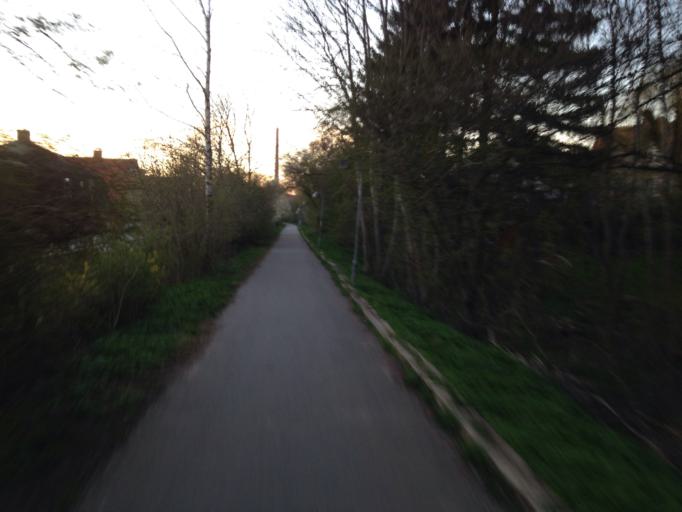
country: DK
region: Capital Region
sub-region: Hillerod Kommune
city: Hillerod
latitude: 55.9252
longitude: 12.3040
